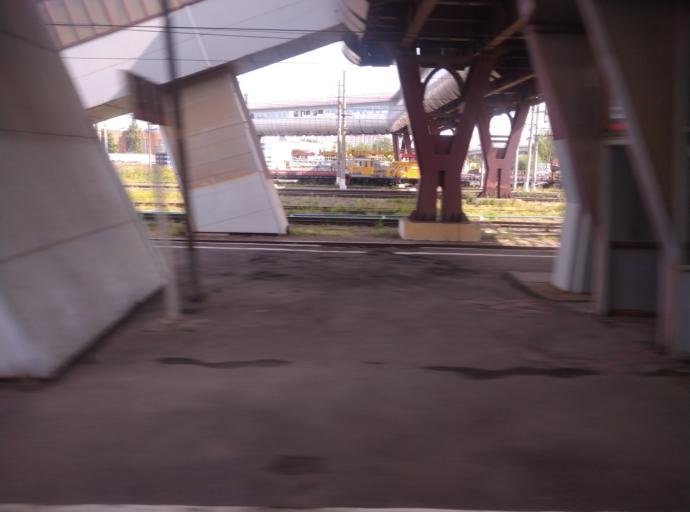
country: RU
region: St.-Petersburg
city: Obukhovo
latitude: 59.8477
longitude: 30.4556
